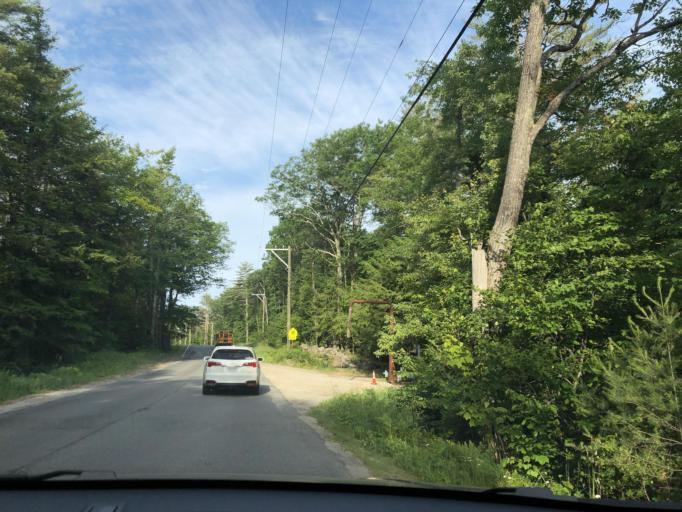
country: US
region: New Hampshire
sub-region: Merrimack County
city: Sutton
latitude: 43.3485
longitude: -71.9315
